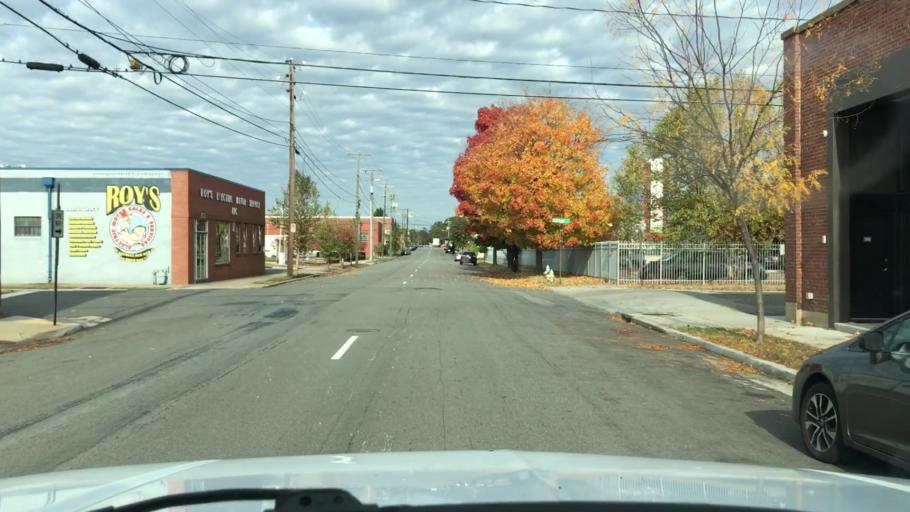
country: US
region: Virginia
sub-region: City of Richmond
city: Richmond
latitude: 37.5693
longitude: -77.4700
